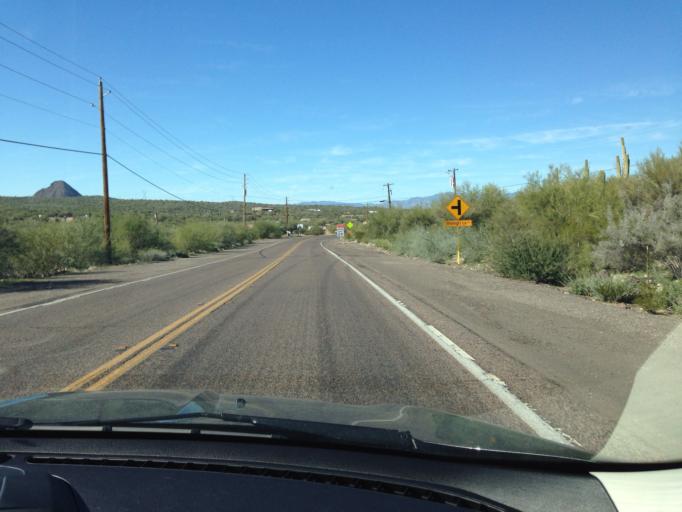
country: US
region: Arizona
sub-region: Maricopa County
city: New River
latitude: 33.8926
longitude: -112.0752
